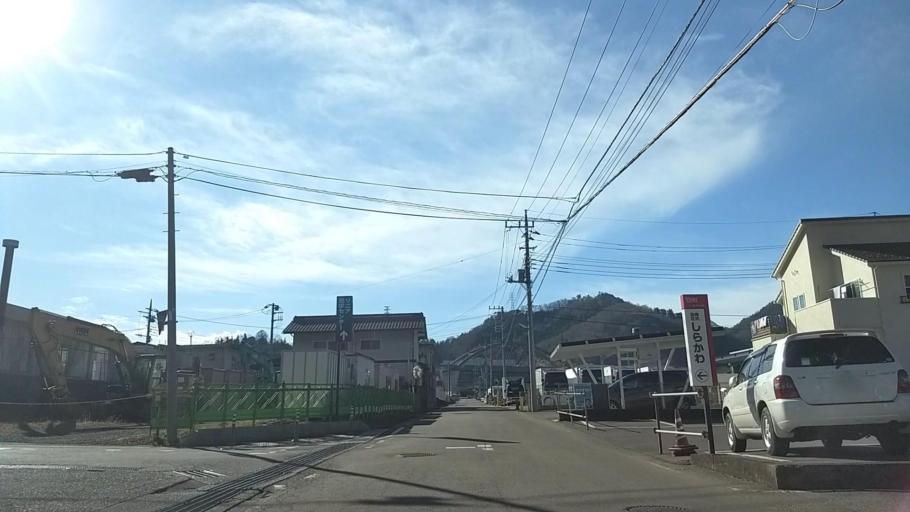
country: JP
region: Yamanashi
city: Otsuki
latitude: 35.5849
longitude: 138.9355
